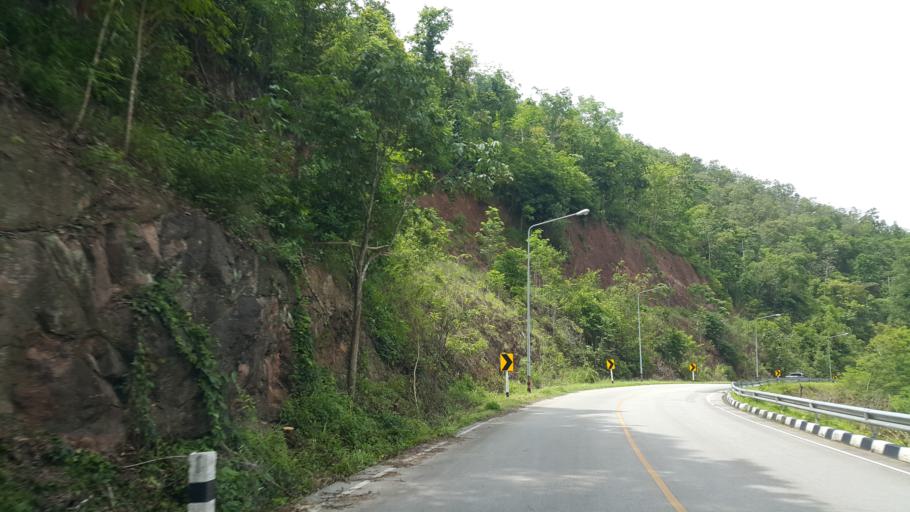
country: TH
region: Lampang
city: Mueang Pan
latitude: 18.7757
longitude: 99.5340
